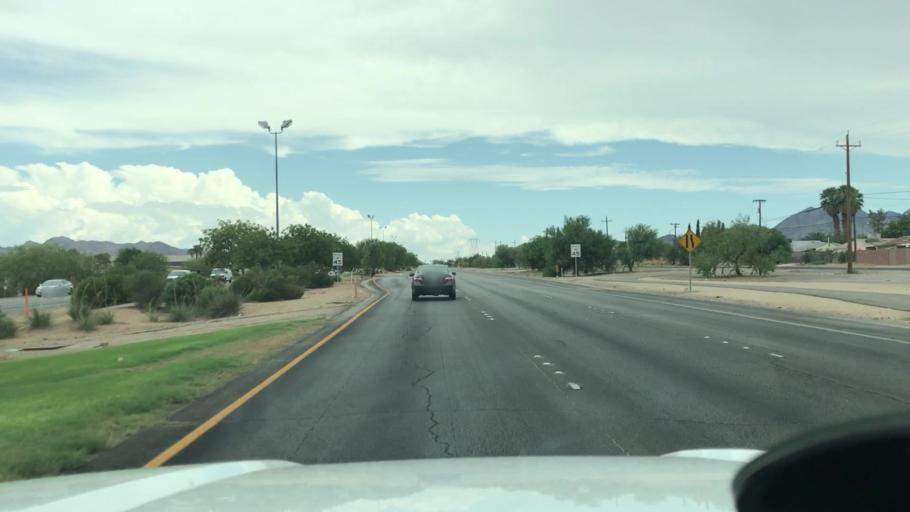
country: US
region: Nevada
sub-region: Clark County
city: Henderson
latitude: 36.0293
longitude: -114.9707
